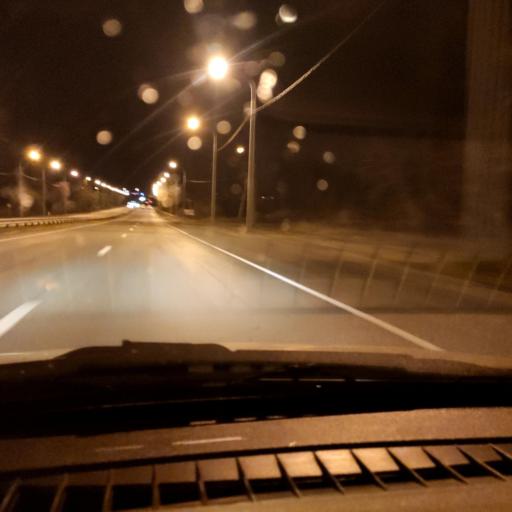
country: RU
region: Samara
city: Zhigulevsk
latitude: 53.5315
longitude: 49.5179
